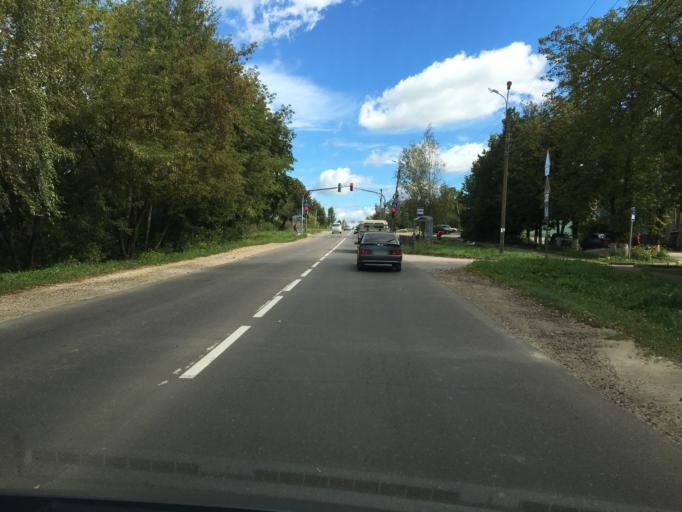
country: RU
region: Kaluga
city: Kaluga
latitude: 54.5454
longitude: 36.3282
